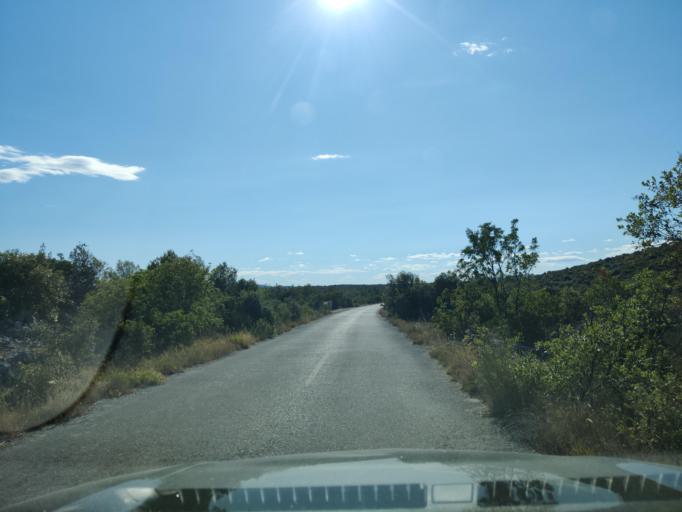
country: HR
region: Sibensko-Kniniska
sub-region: Grad Sibenik
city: Sibenik
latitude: 43.7391
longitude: 15.8672
